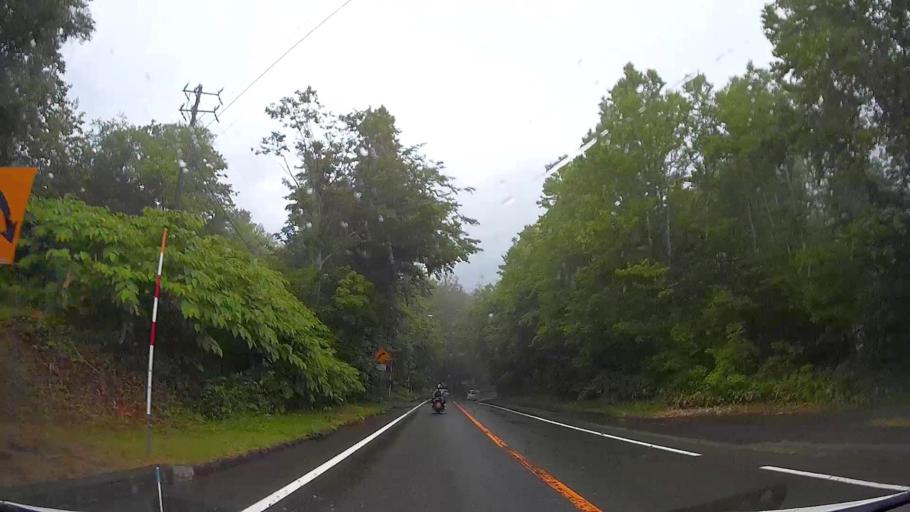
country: JP
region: Hokkaido
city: Shiraoi
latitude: 42.7671
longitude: 141.4154
